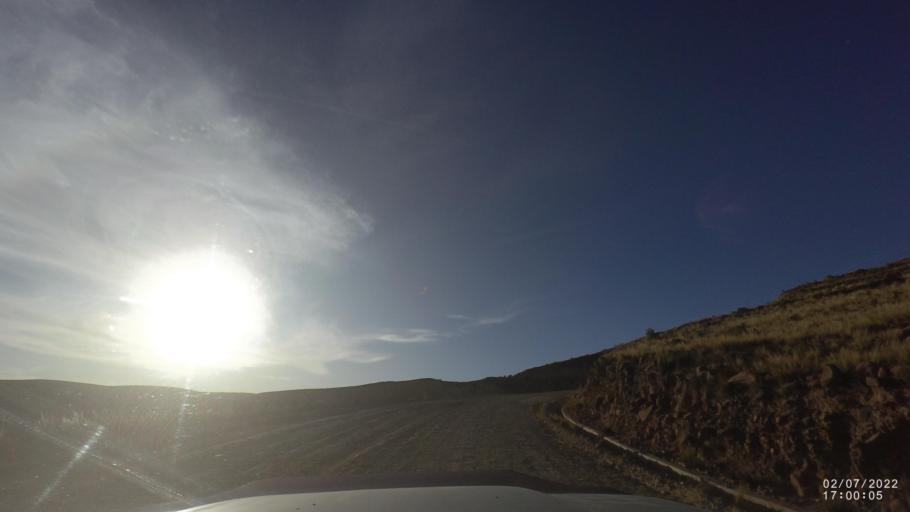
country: BO
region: Cochabamba
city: Irpa Irpa
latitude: -17.9395
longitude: -66.5536
